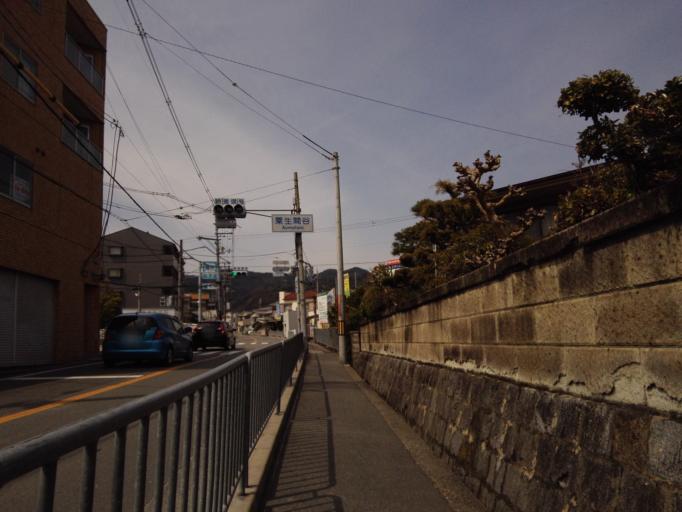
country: JP
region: Osaka
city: Mino
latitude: 34.8469
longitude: 135.5138
